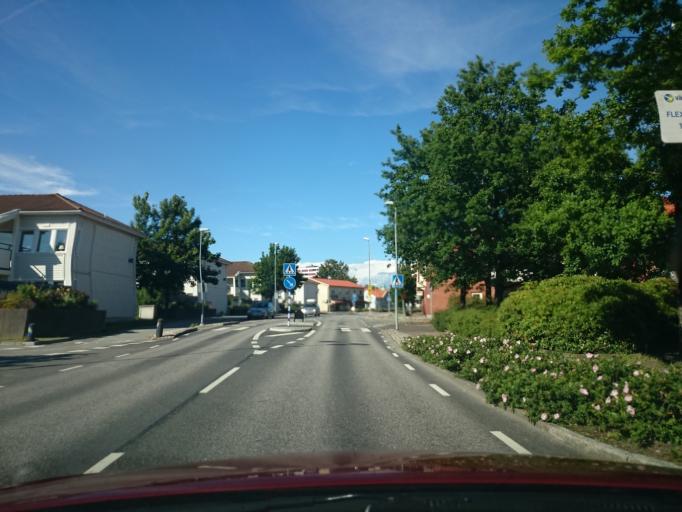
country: SE
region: Vaestra Goetaland
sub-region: Lerums Kommun
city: Lerum
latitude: 57.7688
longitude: 12.2659
